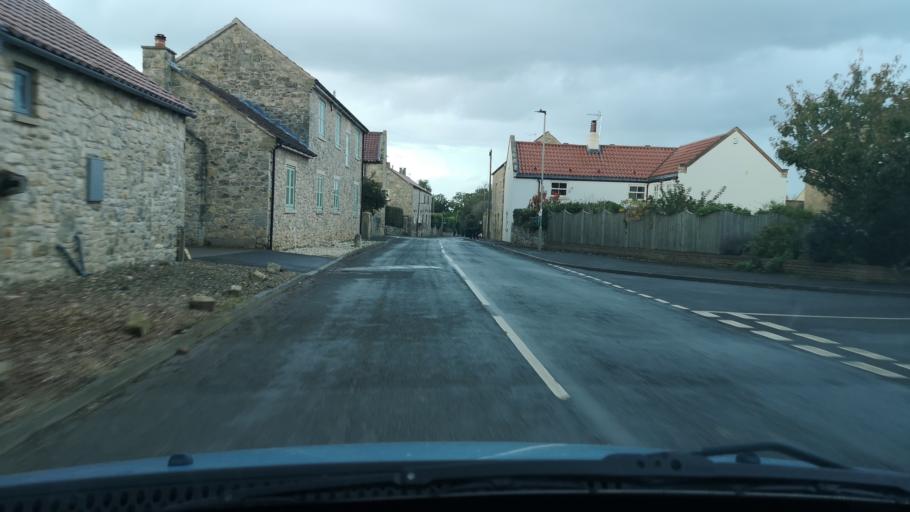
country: GB
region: England
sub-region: Doncaster
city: Norton
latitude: 53.6422
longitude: -1.2183
